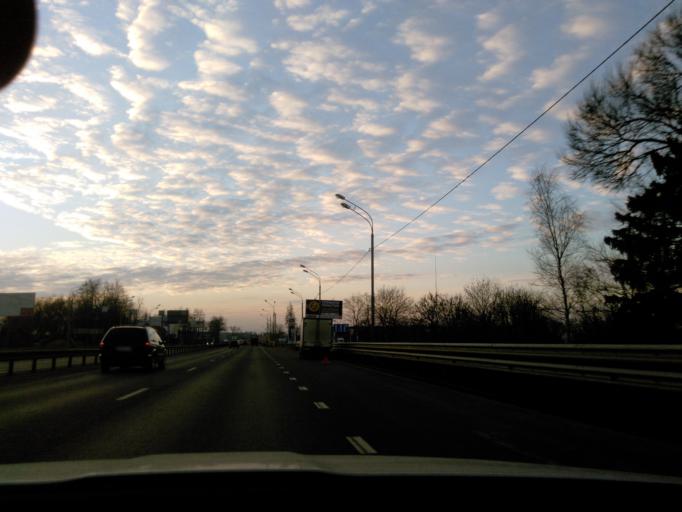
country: RU
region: Moskovskaya
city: Skhodnya
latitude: 55.9774
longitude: 37.3015
